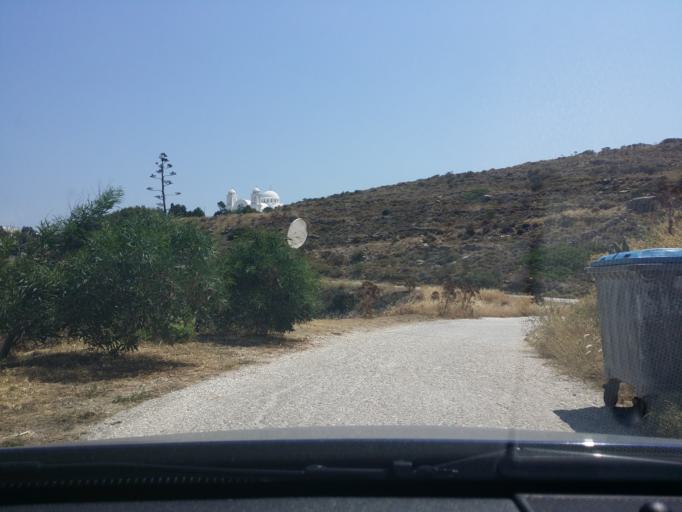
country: GR
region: South Aegean
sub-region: Nomos Kykladon
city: Paros
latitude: 37.0502
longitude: 25.1290
